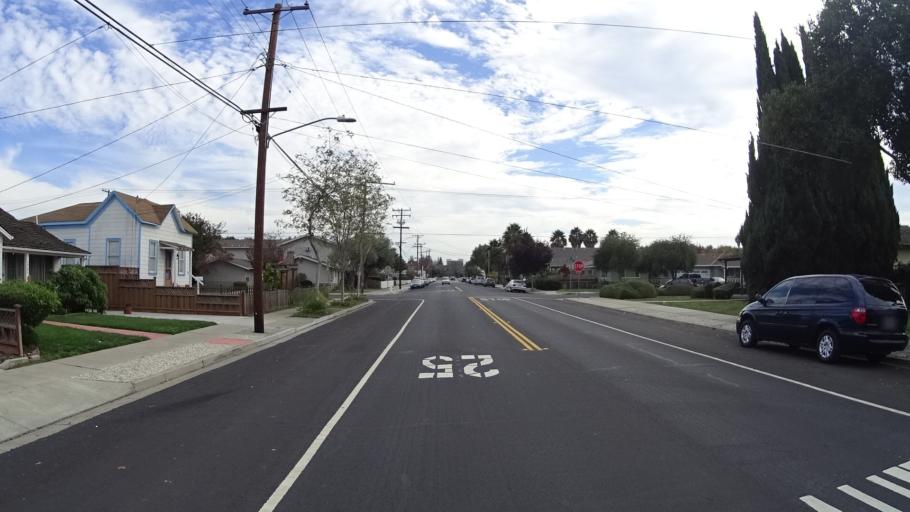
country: US
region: California
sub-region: Santa Clara County
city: Santa Clara
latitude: 37.3562
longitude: -121.9495
